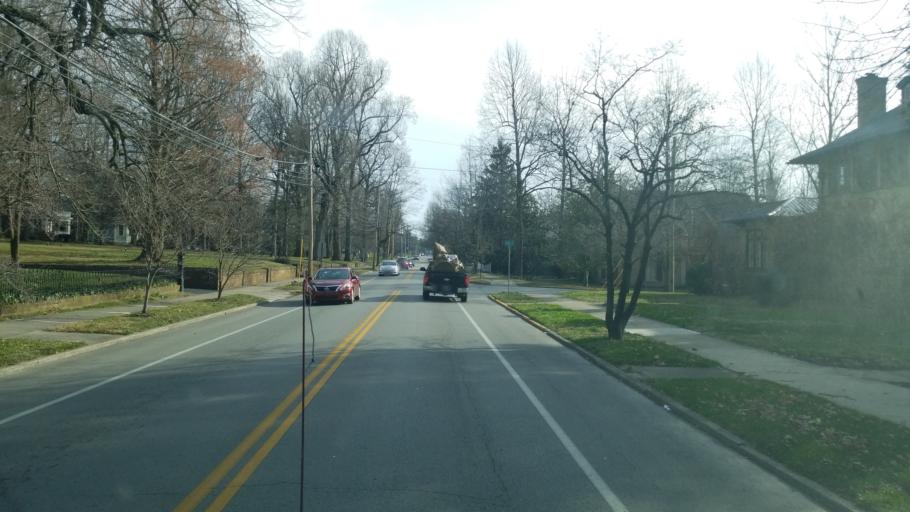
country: US
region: Kentucky
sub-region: Boyle County
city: Danville
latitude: 37.6489
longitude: -84.7712
